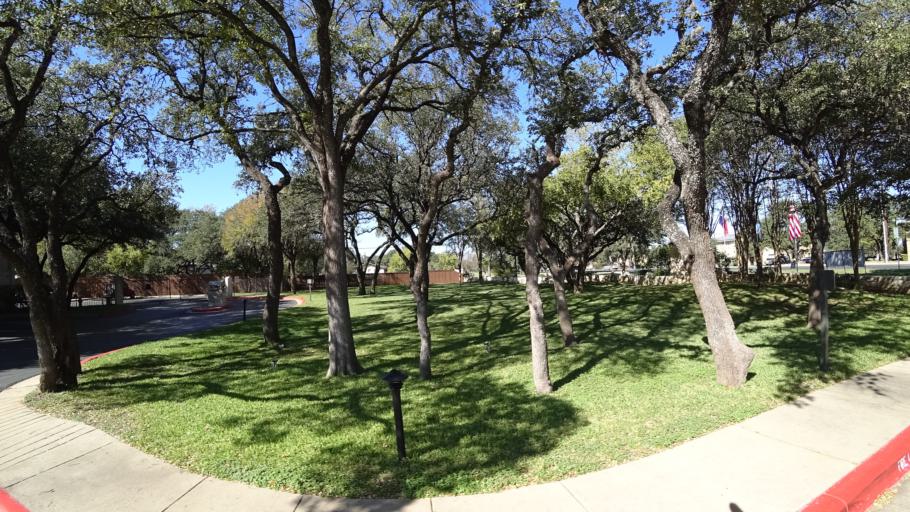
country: US
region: Texas
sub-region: Williamson County
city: Jollyville
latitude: 30.4170
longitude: -97.7504
